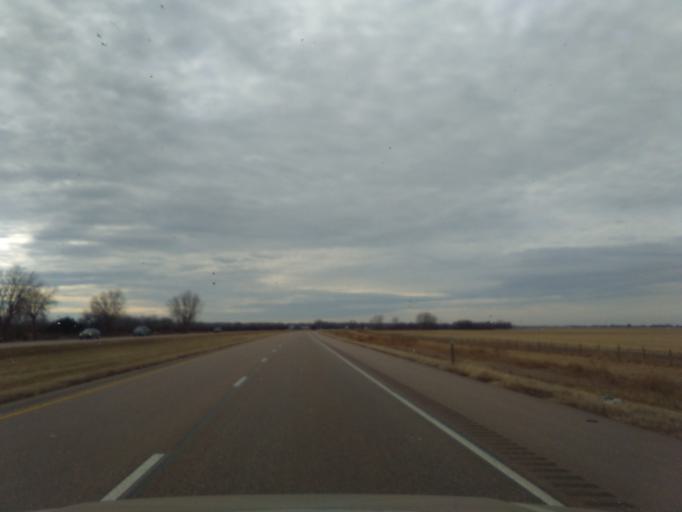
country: US
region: Nebraska
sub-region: Hall County
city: Wood River
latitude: 40.7491
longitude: -98.6188
